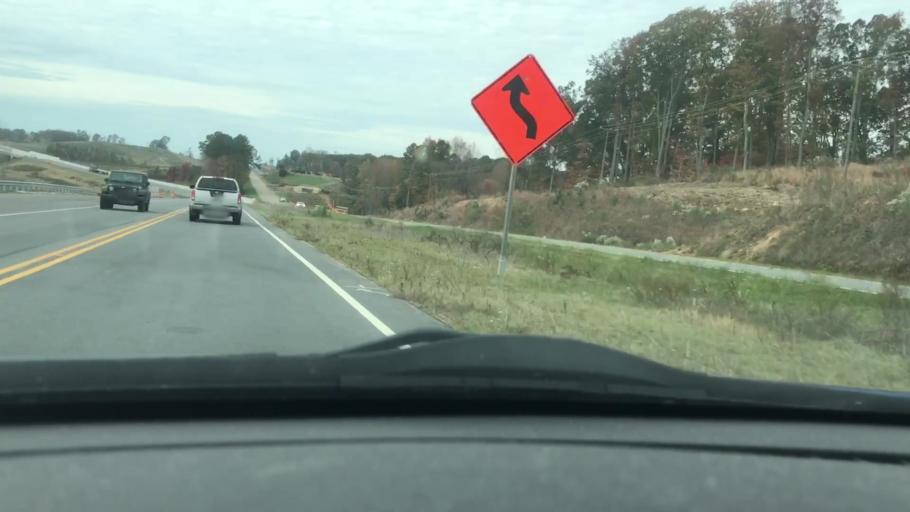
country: US
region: North Carolina
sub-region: Randolph County
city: Asheboro
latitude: 35.6961
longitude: -79.8613
